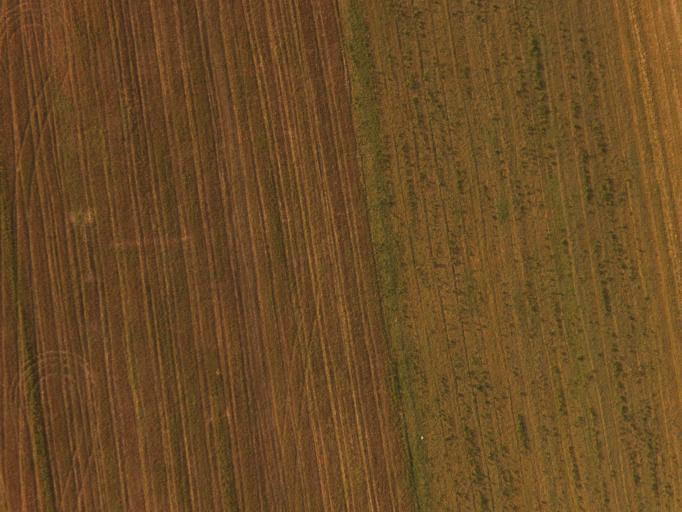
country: HU
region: Somogy
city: Balatonszarszo
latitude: 46.8111
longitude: 17.7886
